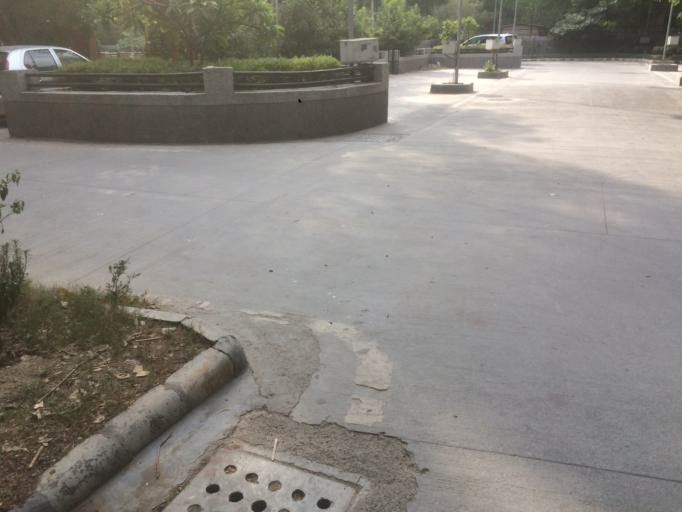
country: IN
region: NCT
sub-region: New Delhi
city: New Delhi
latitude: 28.6269
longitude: 77.2019
